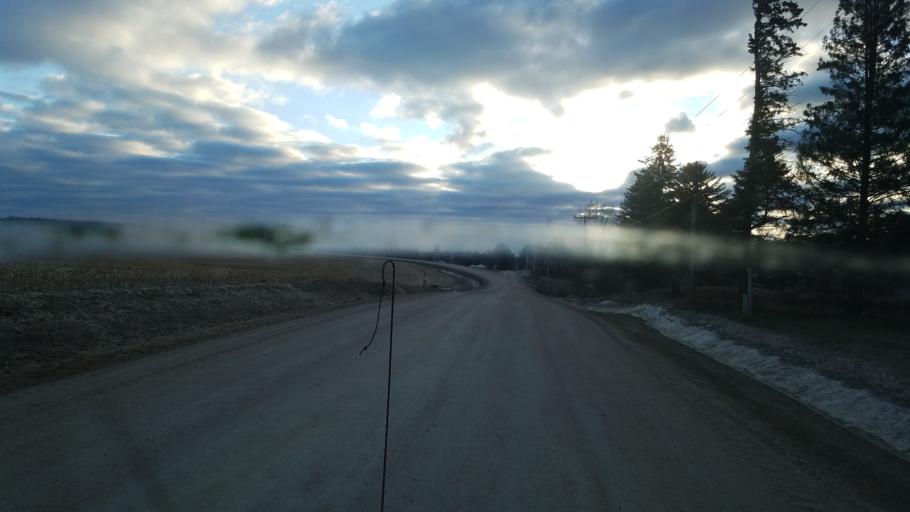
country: US
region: Wisconsin
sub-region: Clark County
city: Neillsville
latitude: 44.5965
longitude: -90.4612
